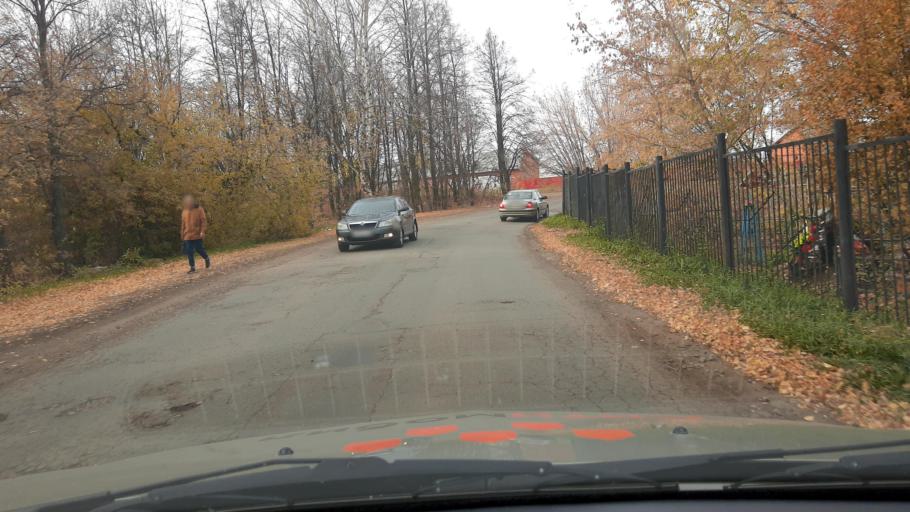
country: RU
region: Bashkortostan
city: Avdon
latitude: 54.7012
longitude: 55.8102
